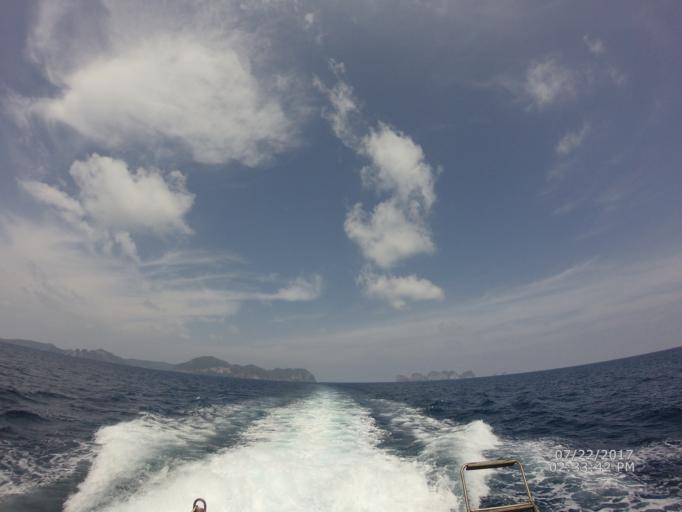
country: TH
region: Phangnga
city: Ban Phru Nai
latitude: 7.7420
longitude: 98.7088
